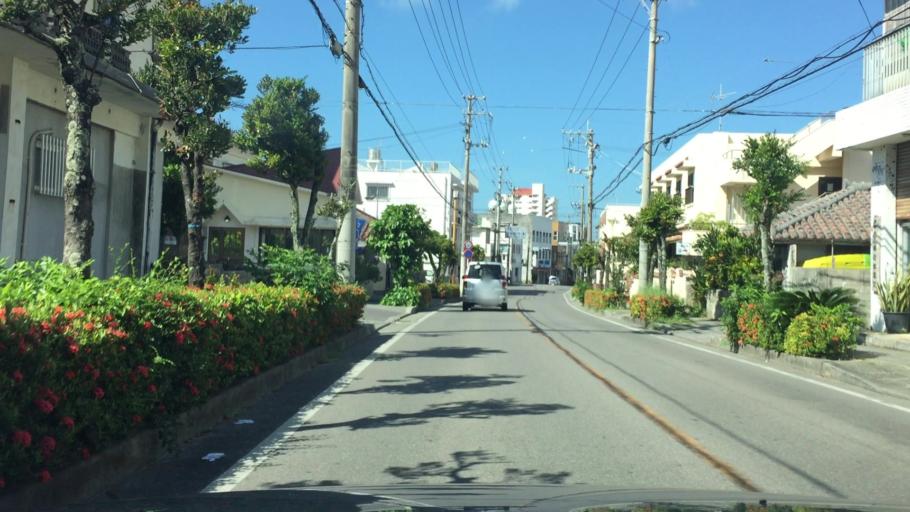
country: JP
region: Okinawa
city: Ishigaki
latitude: 24.3409
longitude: 124.1616
